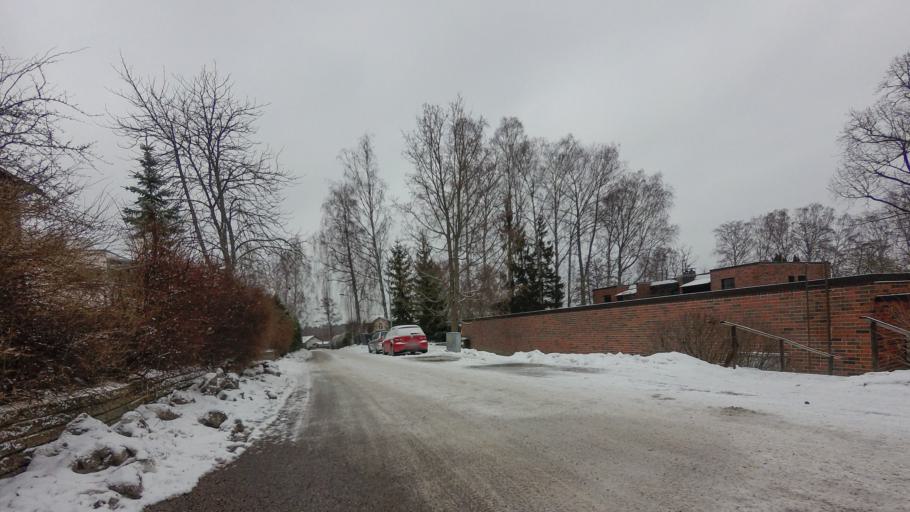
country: FI
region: Uusimaa
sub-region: Helsinki
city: Vantaa
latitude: 60.2018
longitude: 25.0958
